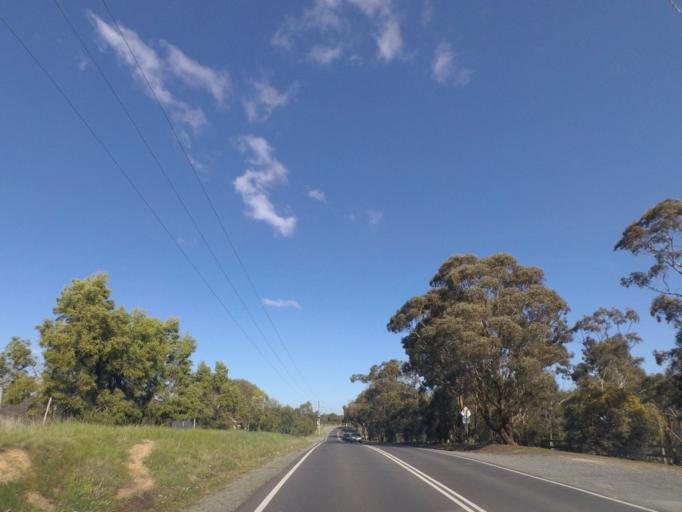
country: AU
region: Victoria
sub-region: Manningham
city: Park Orchards
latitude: -37.7683
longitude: 145.1999
